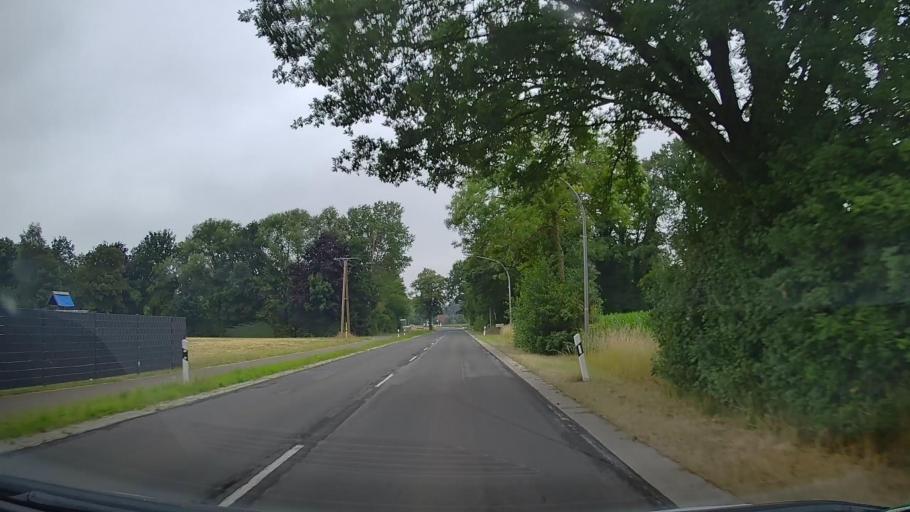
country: DE
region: North Rhine-Westphalia
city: Rahden
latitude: 52.4611
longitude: 8.5848
